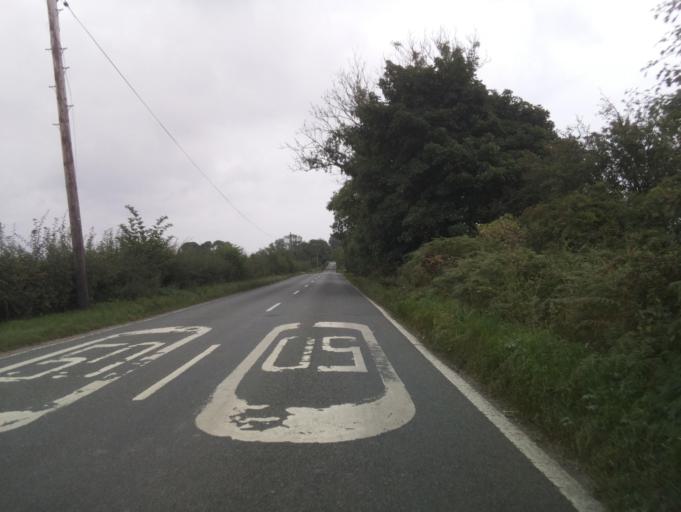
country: GB
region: England
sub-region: Derbyshire
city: Wirksworth
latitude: 53.0179
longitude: -1.5932
